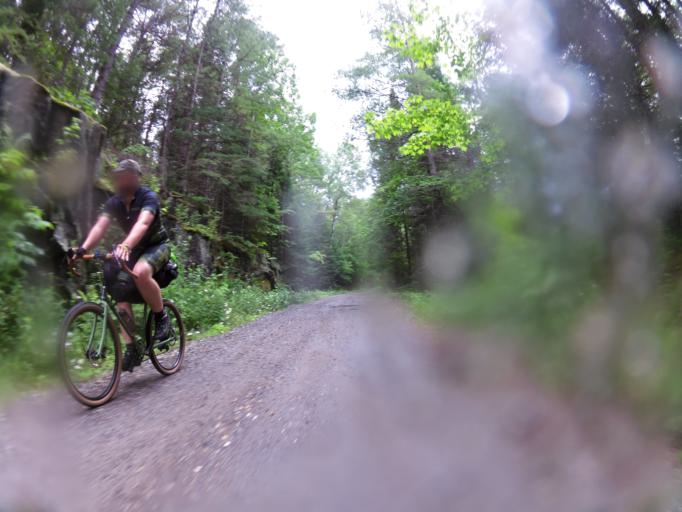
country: CA
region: Ontario
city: Renfrew
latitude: 45.0789
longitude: -76.7200
